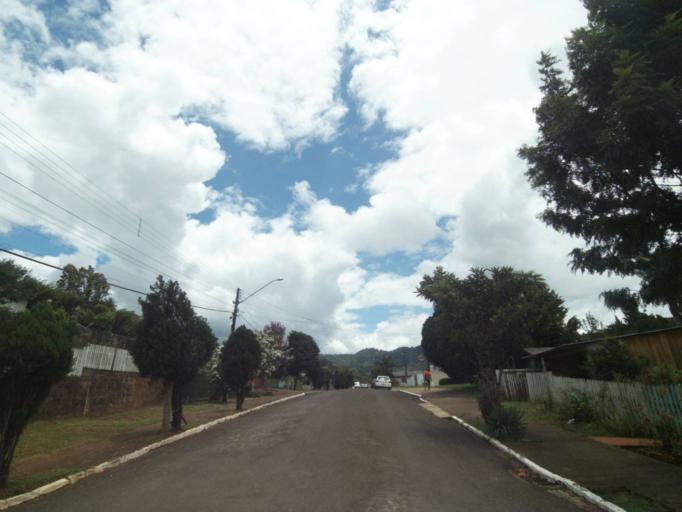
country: BR
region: Parana
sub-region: Pinhao
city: Pinhao
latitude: -26.1585
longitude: -51.5579
